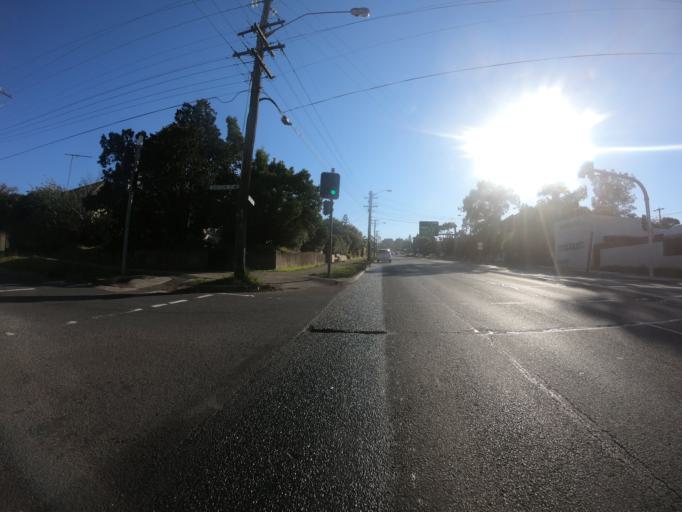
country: AU
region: New South Wales
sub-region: Canada Bay
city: Rhodes
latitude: -33.8193
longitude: 151.0998
